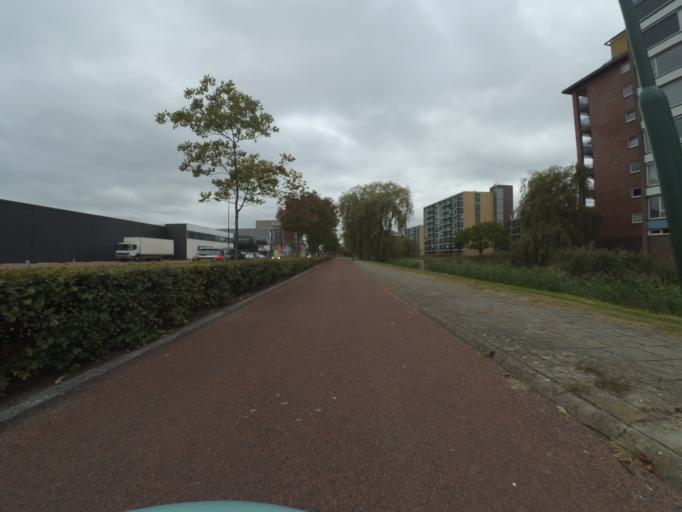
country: NL
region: Utrecht
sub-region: Gemeente Veenendaal
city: Veenendaal
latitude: 52.0165
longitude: 5.5606
